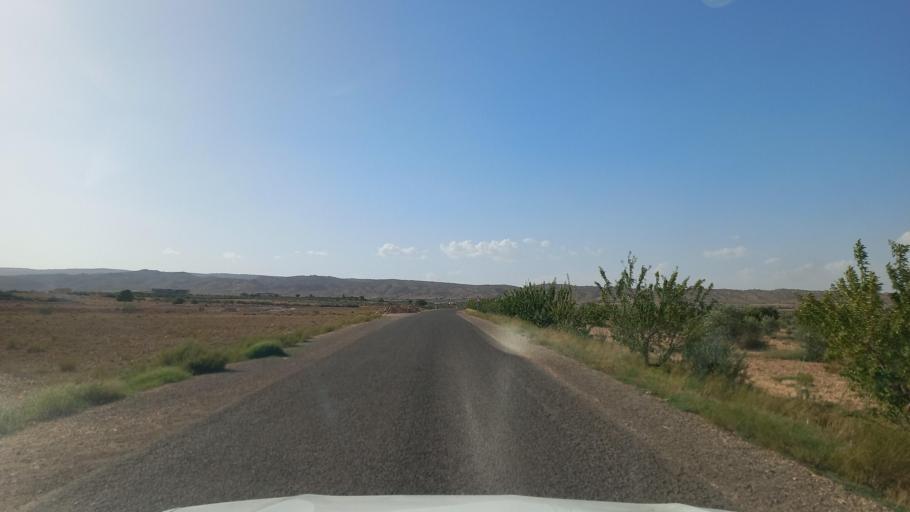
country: TN
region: Al Qasrayn
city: Sbiba
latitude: 35.3346
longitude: 9.0027
